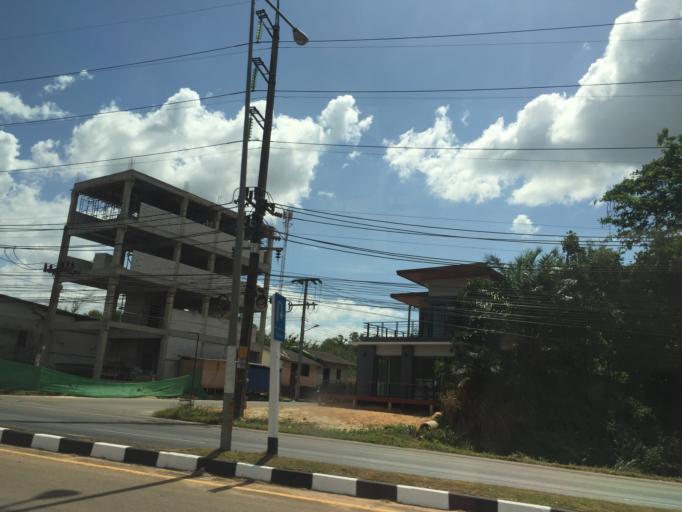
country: TH
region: Krabi
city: Krabi
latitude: 8.1027
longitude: 98.8912
